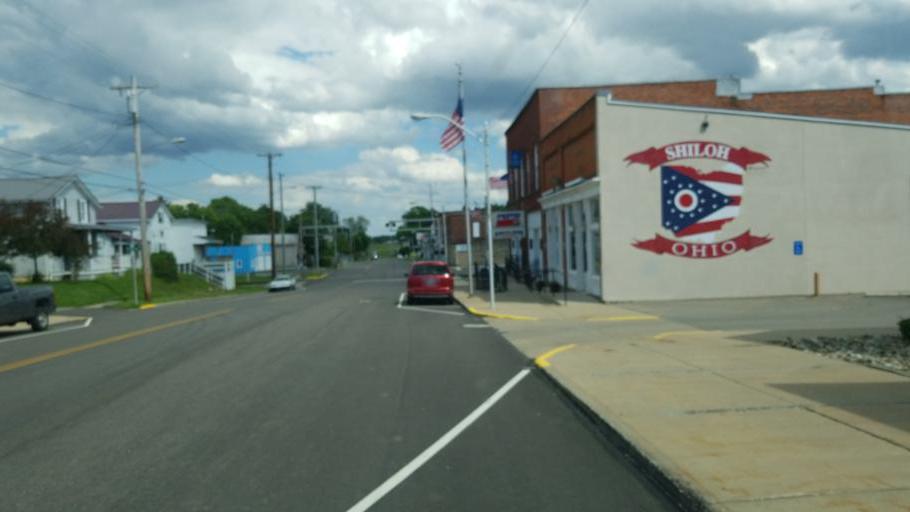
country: US
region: Ohio
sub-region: Huron County
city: Plymouth
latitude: 40.9674
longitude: -82.6021
